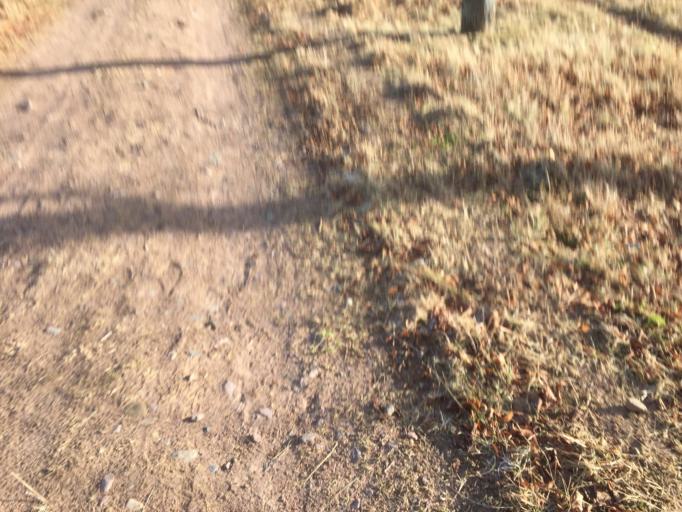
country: SE
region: Joenkoeping
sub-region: Aneby Kommun
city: Aneby
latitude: 57.8254
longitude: 14.8233
